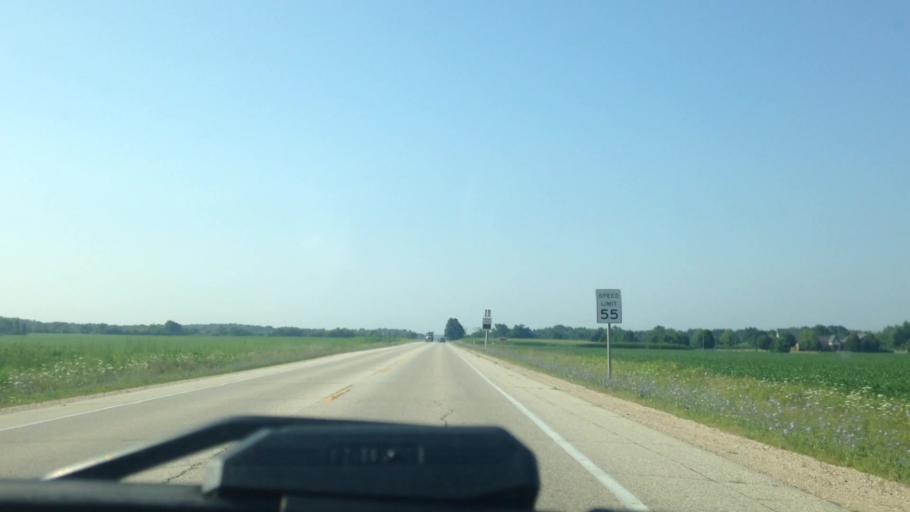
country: US
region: Wisconsin
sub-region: Washington County
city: Richfield
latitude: 43.2218
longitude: -88.2618
